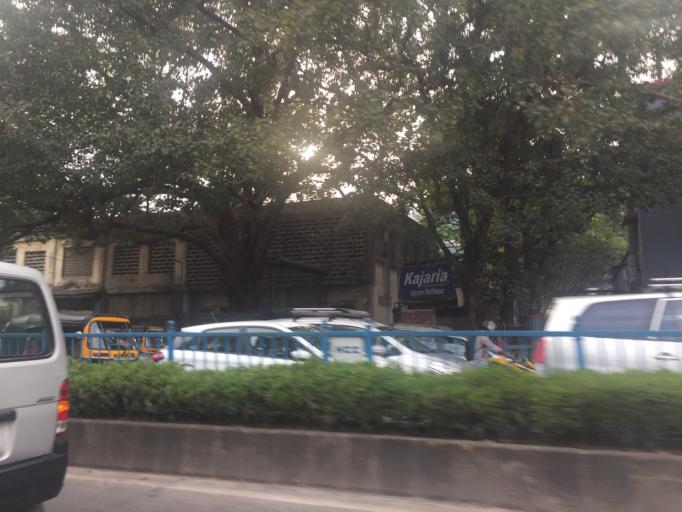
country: IN
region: Maharashtra
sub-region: Mumbai Suburban
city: Powai
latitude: 19.1237
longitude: 72.9253
